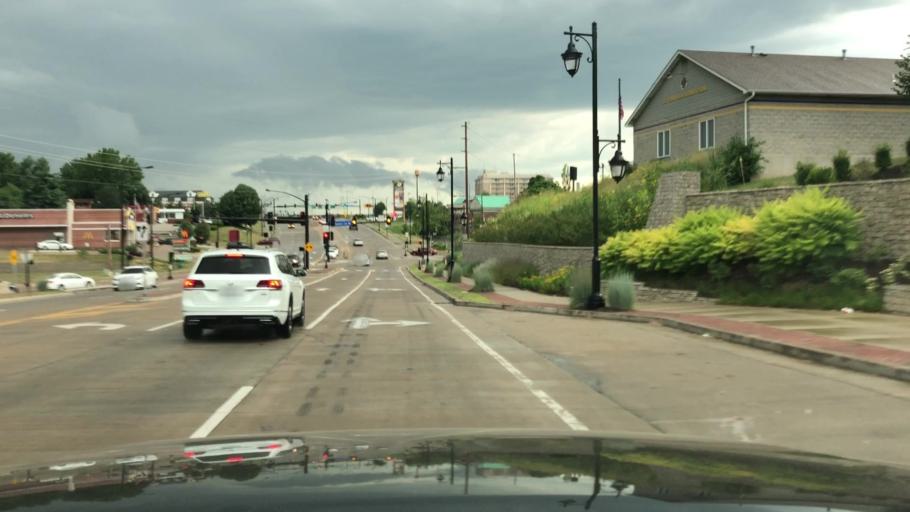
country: US
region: Missouri
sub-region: Saint Charles County
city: Saint Charles
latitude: 38.7739
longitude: -90.4911
